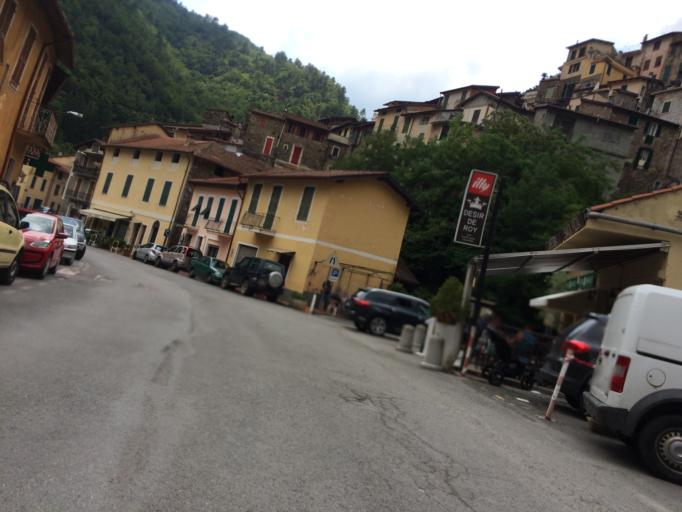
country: IT
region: Liguria
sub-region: Provincia di Imperia
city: Pigna
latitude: 43.9324
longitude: 7.6647
